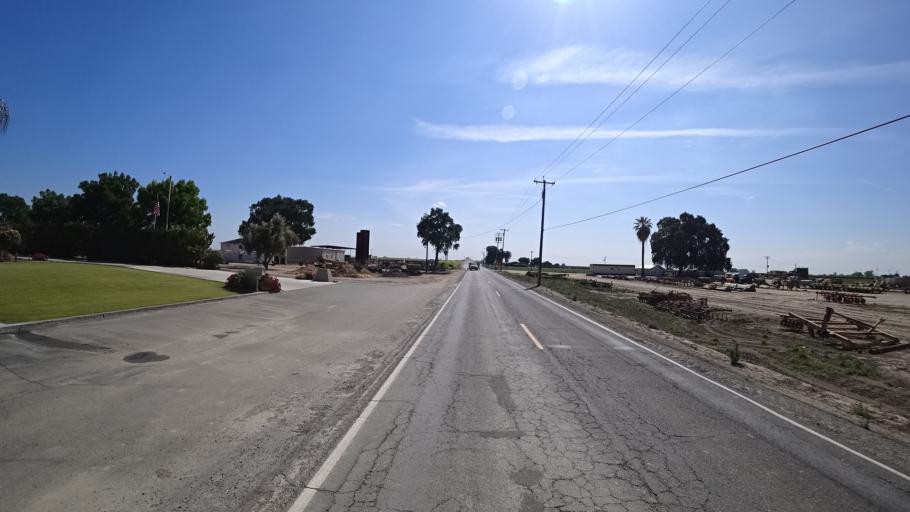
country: US
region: California
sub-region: Kings County
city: Lemoore
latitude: 36.2549
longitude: -119.7480
